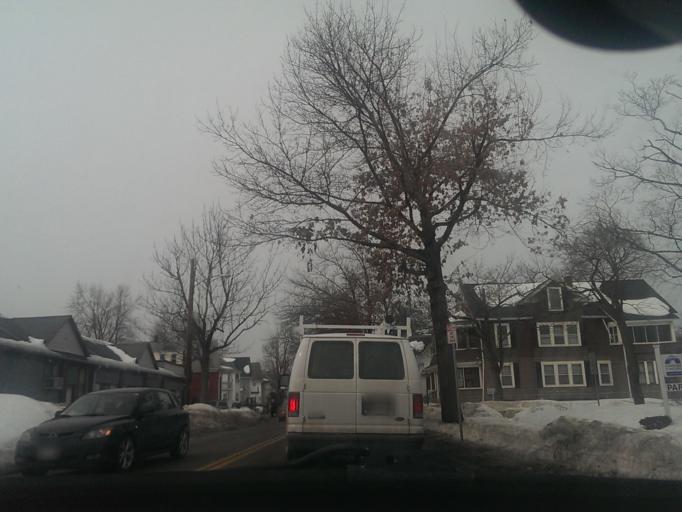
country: US
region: Massachusetts
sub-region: Hampden County
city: East Longmeadow
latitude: 42.0839
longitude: -72.5439
